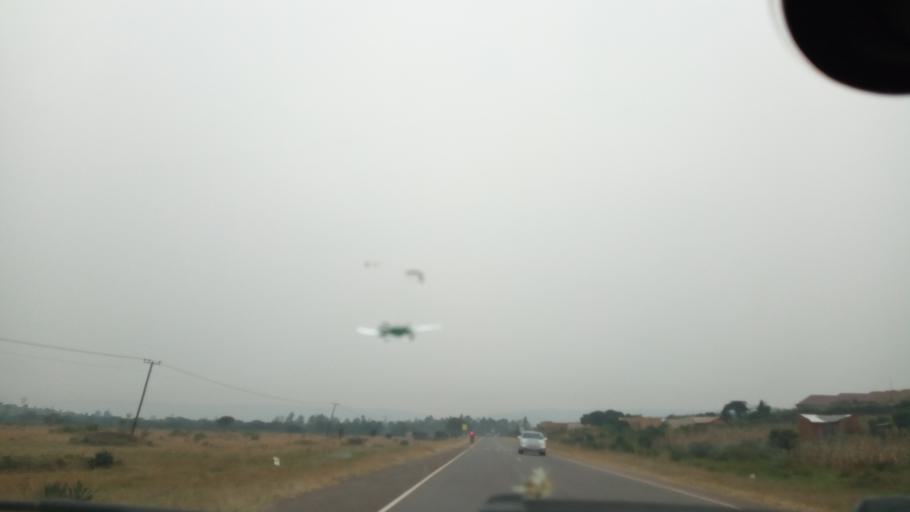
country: UG
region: Western Region
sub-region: Mbarara District
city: Mbarara
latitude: -0.7258
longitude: 30.7307
